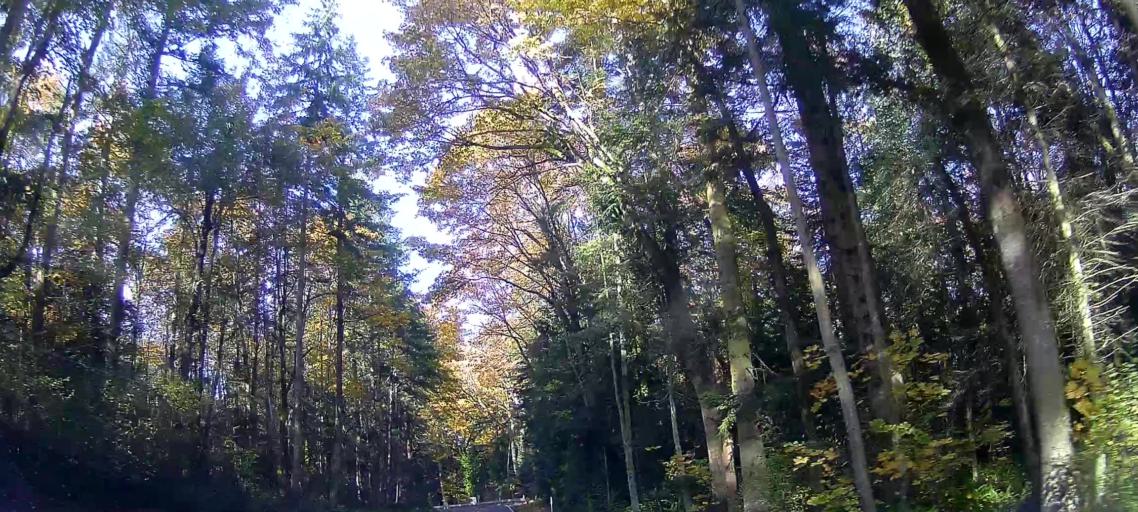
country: US
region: Washington
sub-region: Snohomish County
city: Stanwood
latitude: 48.2304
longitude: -122.4557
